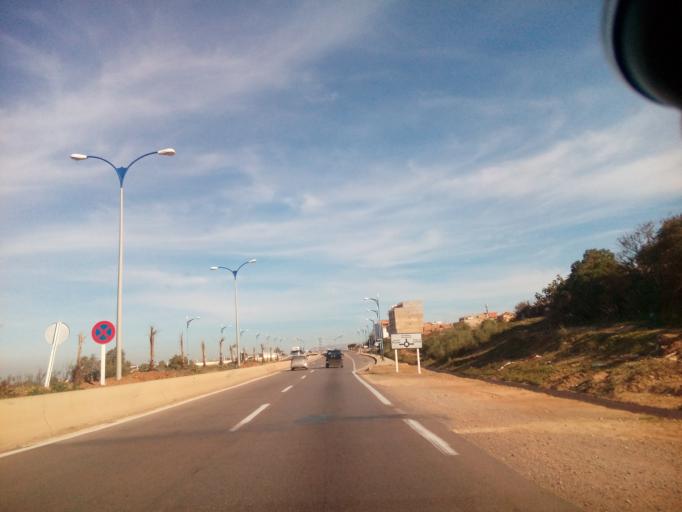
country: DZ
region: Mostaganem
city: Mostaganem
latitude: 35.8662
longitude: 0.0359
